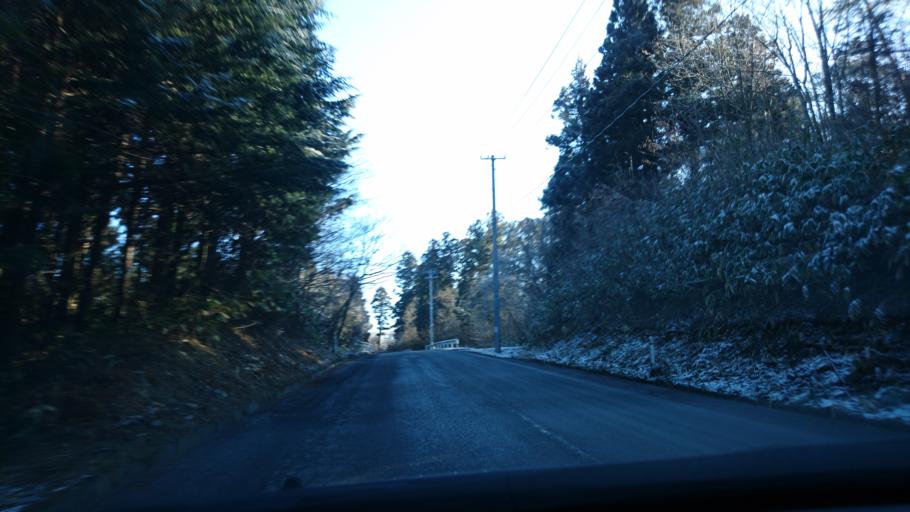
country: JP
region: Iwate
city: Ichinoseki
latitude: 38.8801
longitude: 141.3345
